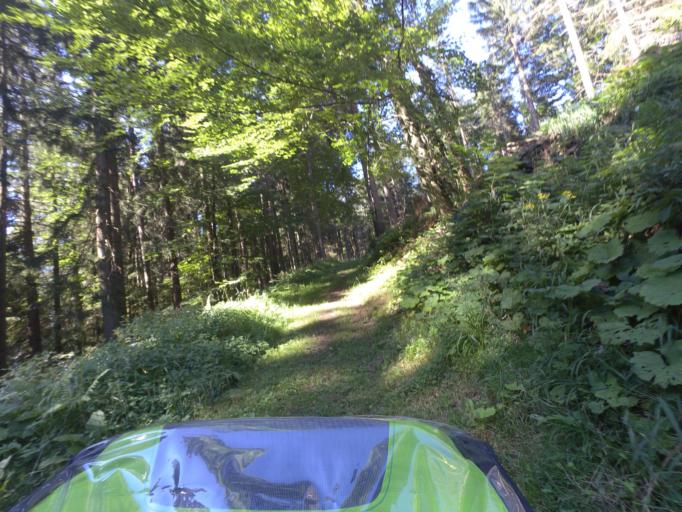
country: AT
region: Salzburg
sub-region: Politischer Bezirk Hallein
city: Hallein
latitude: 47.6561
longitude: 13.1048
